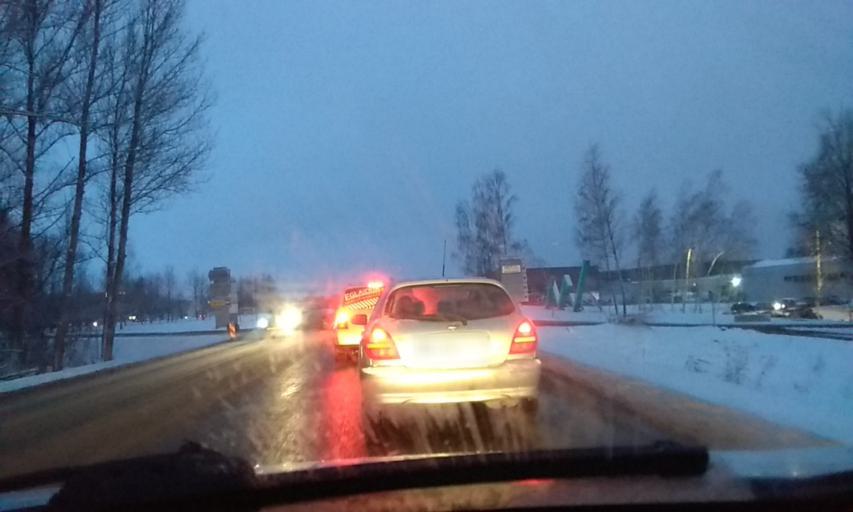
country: LT
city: Ramuciai
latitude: 54.9076
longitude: 24.0307
